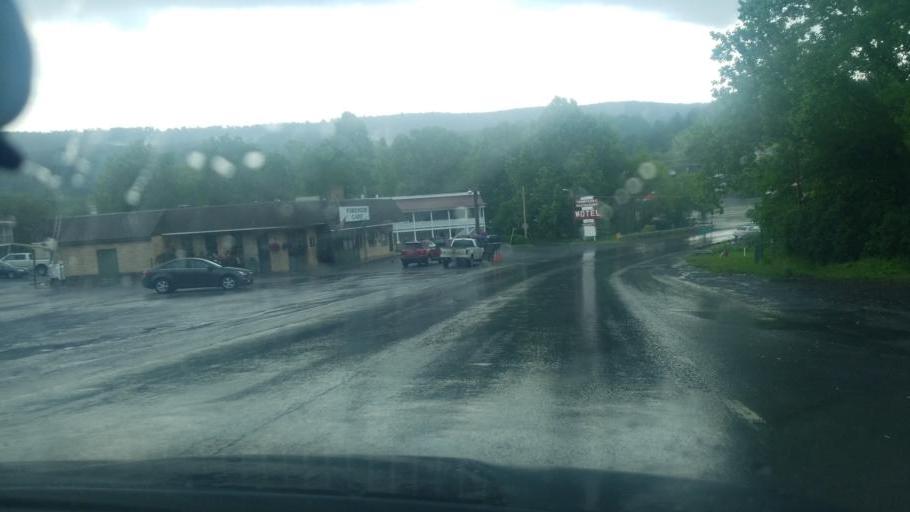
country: US
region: West Virginia
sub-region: Pendleton County
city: Franklin
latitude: 38.6541
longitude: -79.3320
